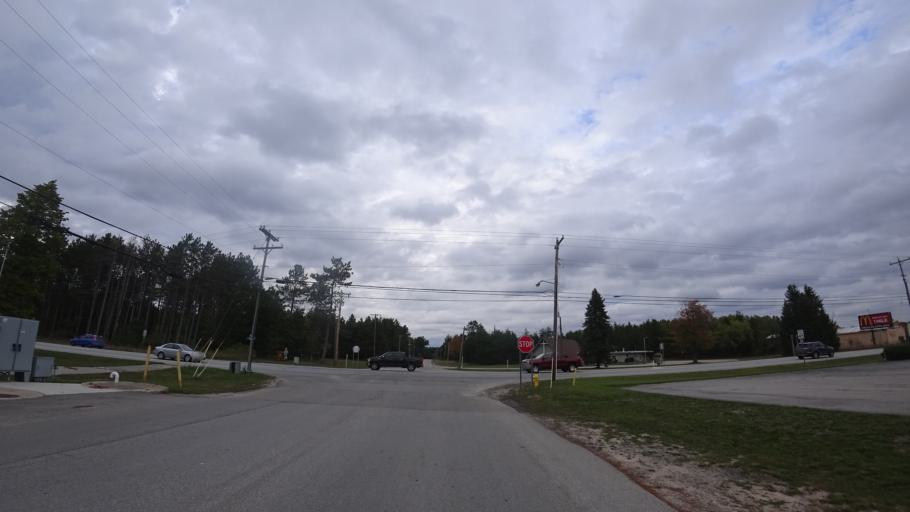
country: US
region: Michigan
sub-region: Kalkaska County
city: Kalkaska
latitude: 44.7424
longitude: -85.1844
